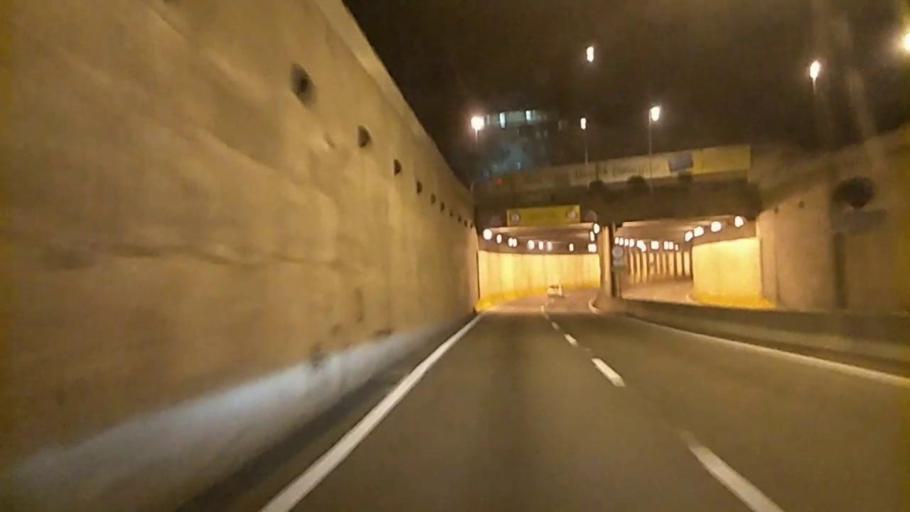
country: MY
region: Selangor
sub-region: Petaling
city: Petaling Jaya
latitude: 3.1330
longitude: 101.6251
